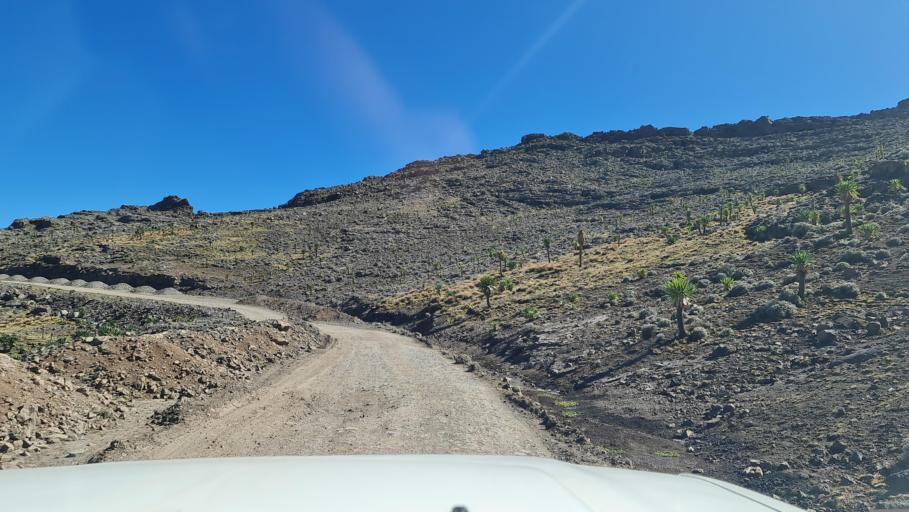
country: ET
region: Amhara
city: Debark'
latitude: 13.2153
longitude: 38.2192
